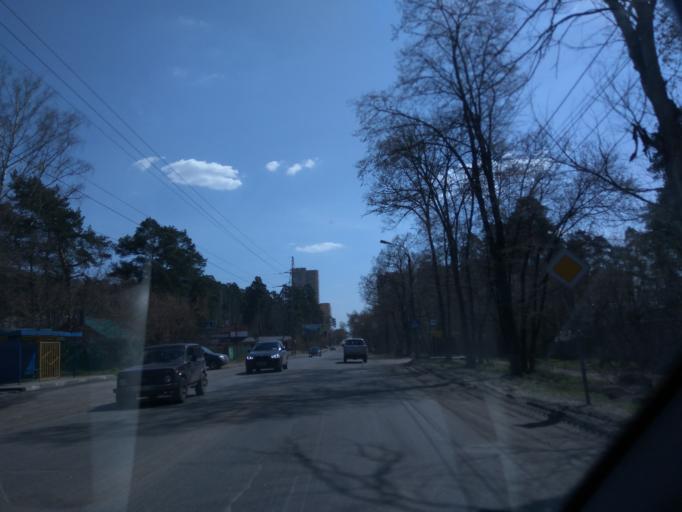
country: RU
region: Moskovskaya
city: Kratovo
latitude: 55.5697
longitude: 38.1906
